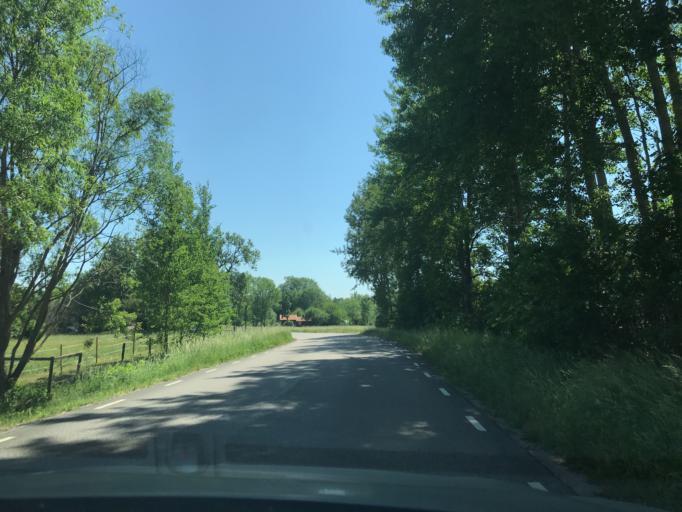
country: SE
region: Vaestra Goetaland
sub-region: Gotene Kommun
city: Kallby
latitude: 58.5349
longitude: 13.3220
